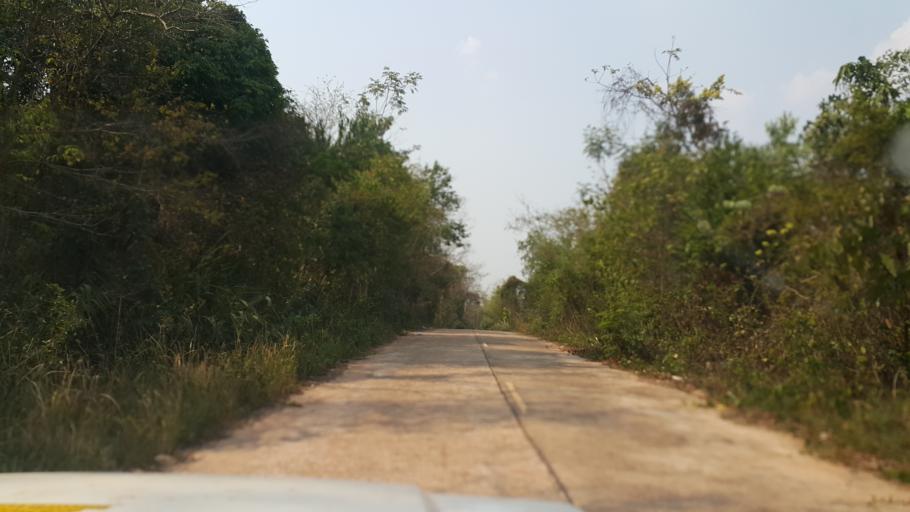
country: TH
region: Nakhon Phanom
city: Ban Phaeng
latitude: 17.9606
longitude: 104.1559
